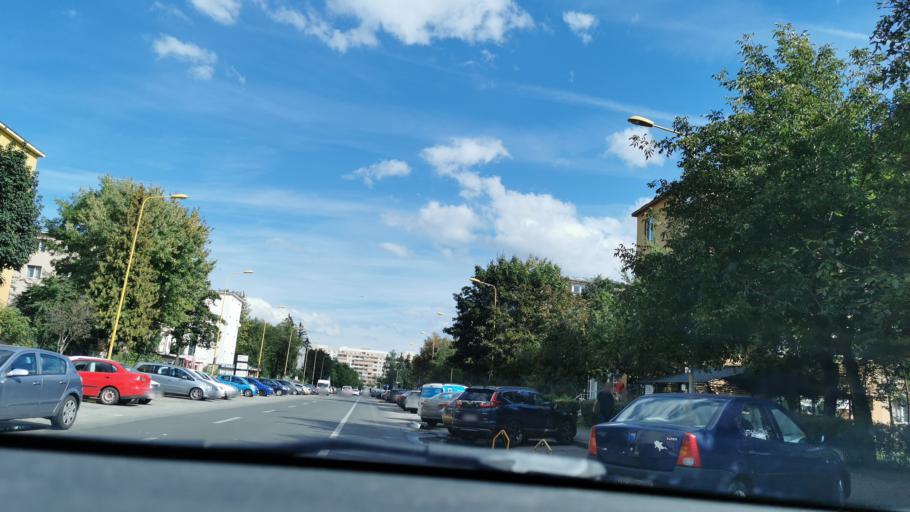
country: RO
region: Brasov
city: Brasov
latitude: 45.6419
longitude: 25.6274
